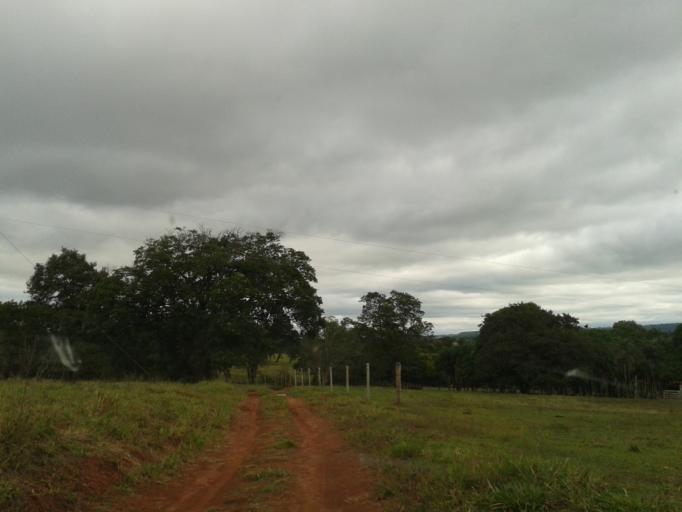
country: BR
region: Minas Gerais
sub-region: Campina Verde
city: Campina Verde
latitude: -19.4853
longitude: -49.6200
